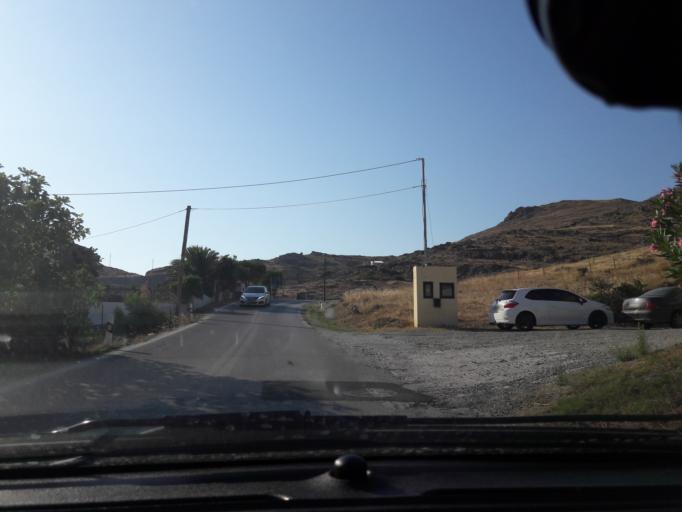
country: GR
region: North Aegean
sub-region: Nomos Lesvou
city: Myrina
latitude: 39.8583
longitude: 25.0834
